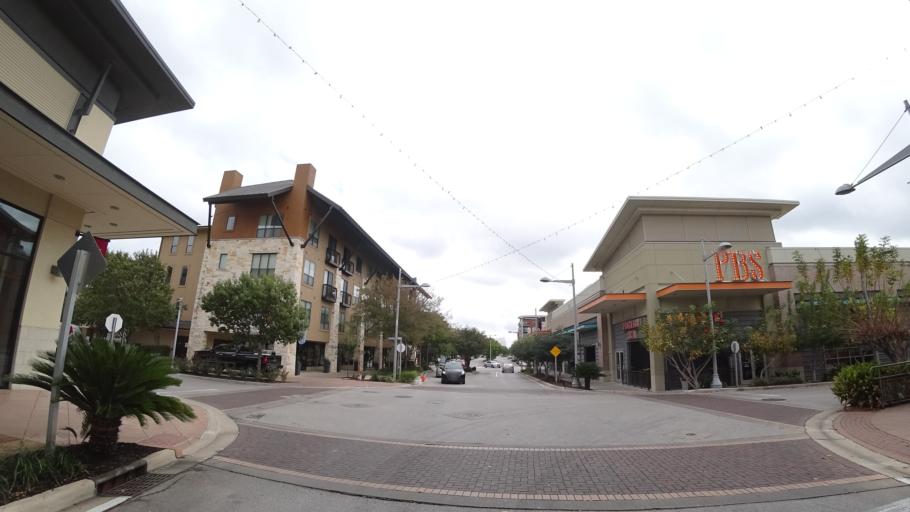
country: US
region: Texas
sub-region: Williamson County
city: Jollyville
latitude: 30.4004
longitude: -97.7259
